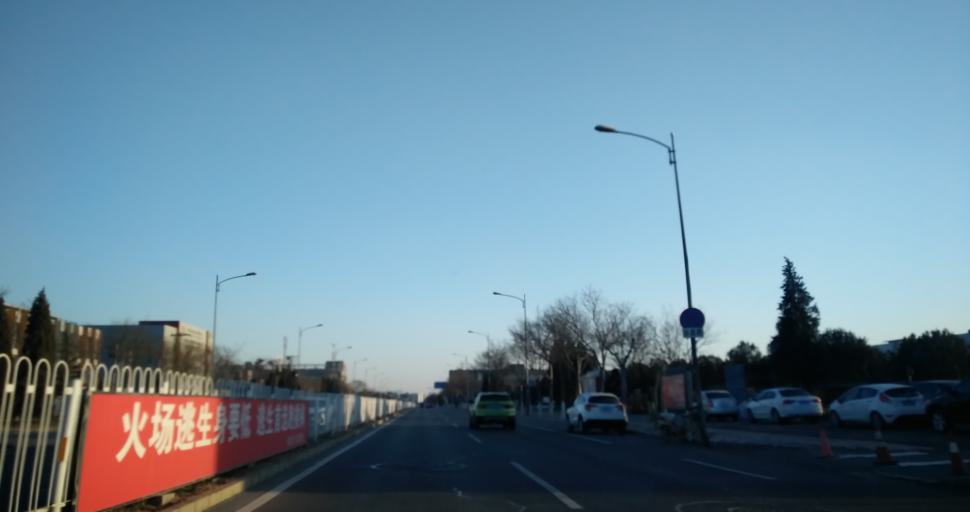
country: CN
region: Beijing
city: Jiugong
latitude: 39.7914
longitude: 116.5137
